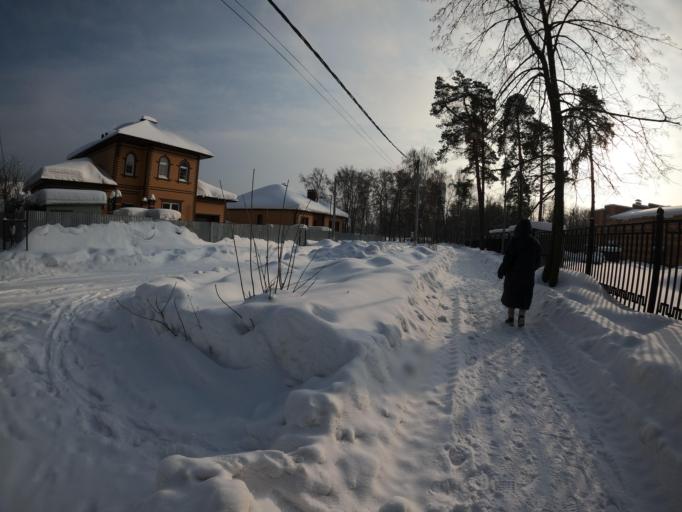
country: RU
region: Moskovskaya
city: Elektrogorsk
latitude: 55.8939
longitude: 38.7758
